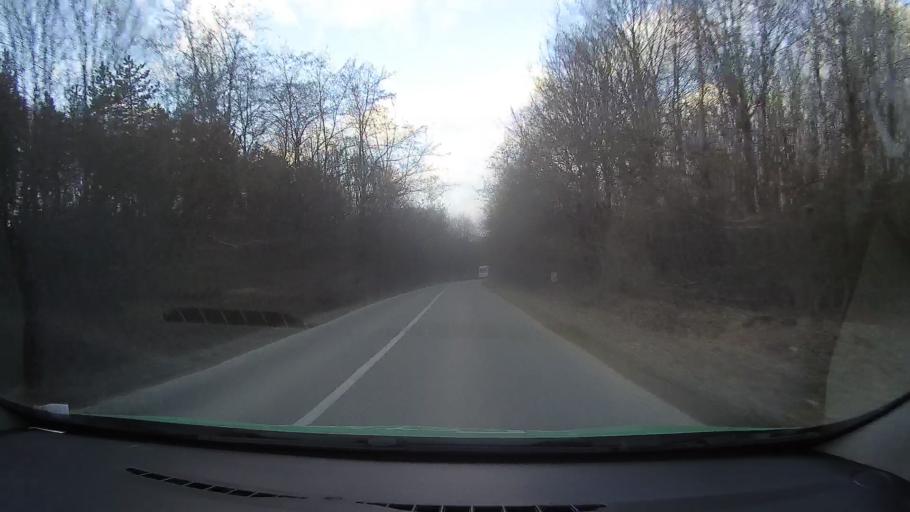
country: RO
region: Dambovita
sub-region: Comuna Gura Ocnitei
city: Gura Ocnitei
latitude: 44.9508
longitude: 25.5957
